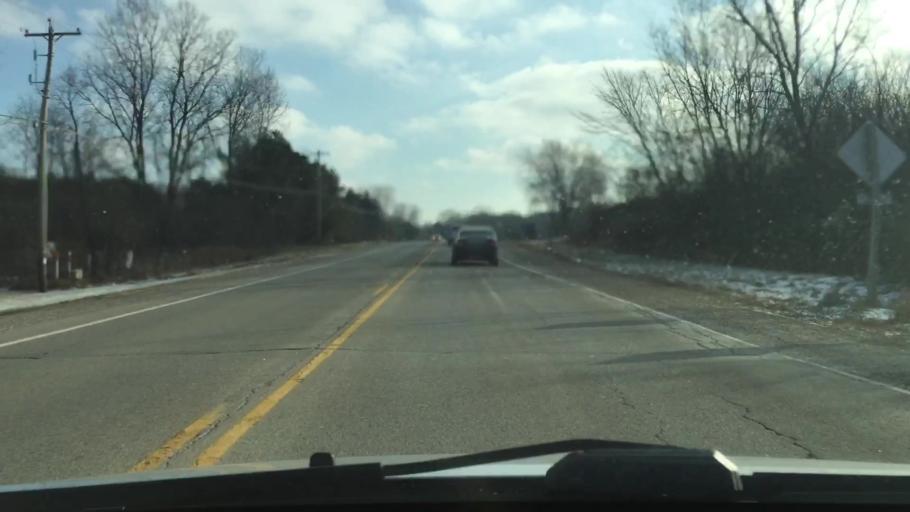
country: US
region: Wisconsin
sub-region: Waukesha County
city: Wales
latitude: 43.0123
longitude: -88.3964
